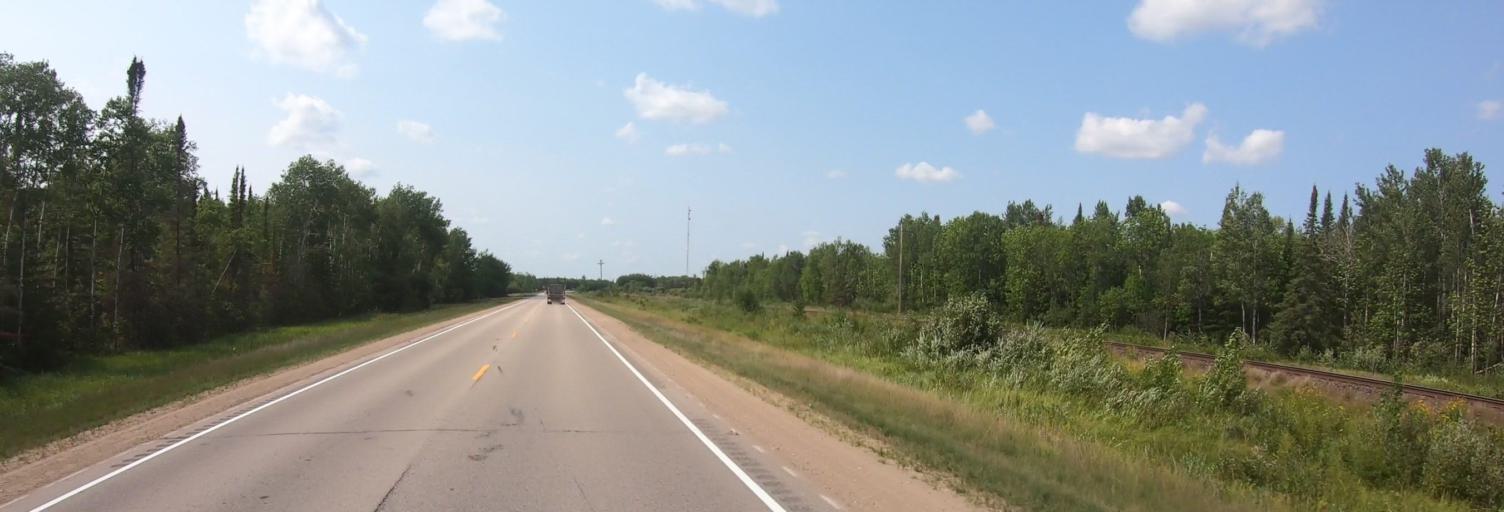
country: US
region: Minnesota
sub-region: Roseau County
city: Warroad
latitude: 48.7952
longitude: -95.0758
